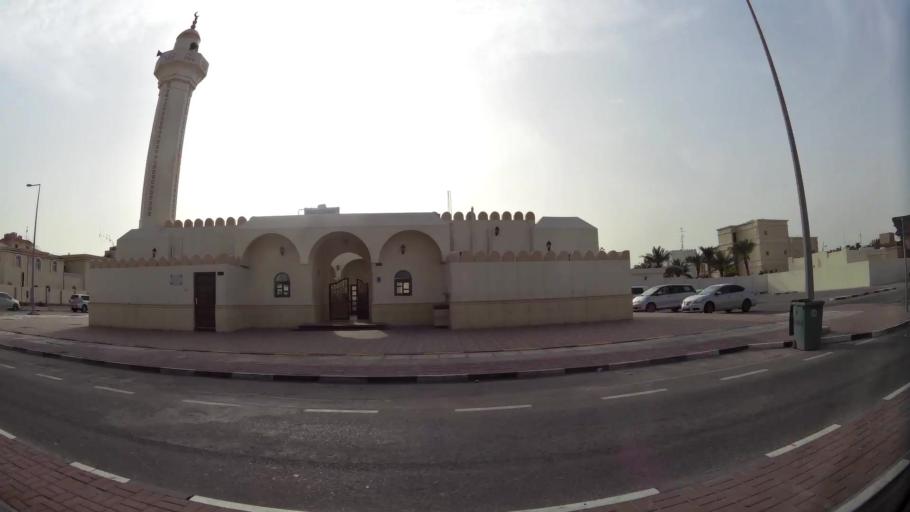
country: QA
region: Baladiyat ad Dawhah
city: Doha
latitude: 25.3260
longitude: 51.5202
